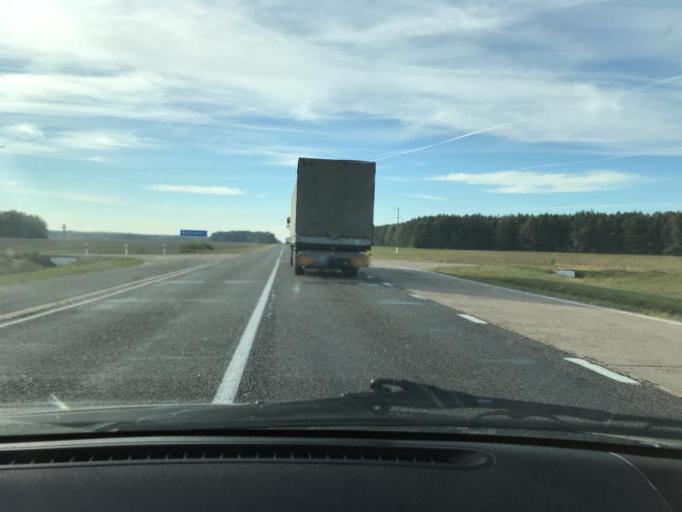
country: BY
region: Brest
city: Lahishyn
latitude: 52.1532
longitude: 25.8167
